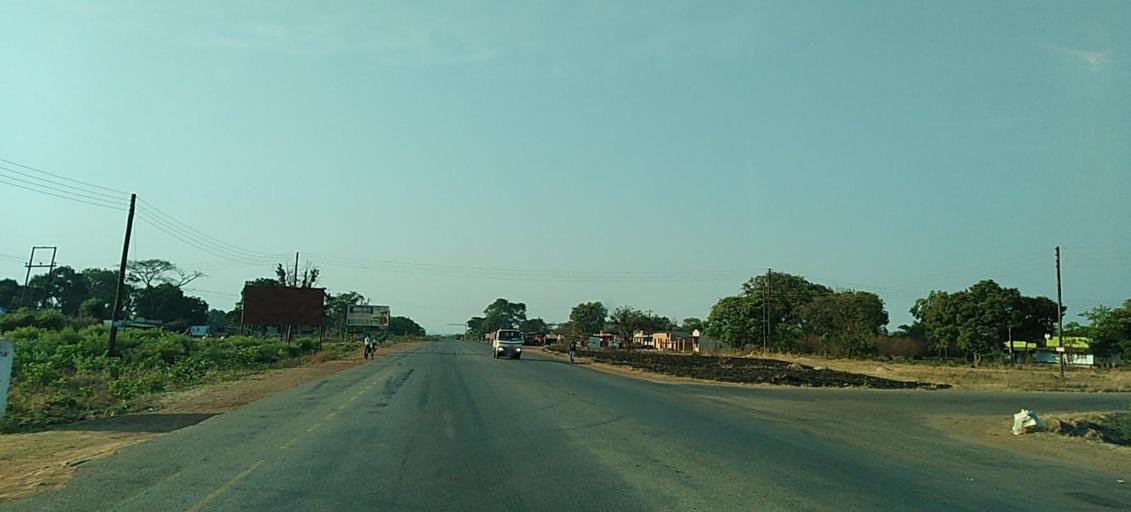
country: ZM
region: Copperbelt
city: Luanshya
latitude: -13.2442
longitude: 28.6781
